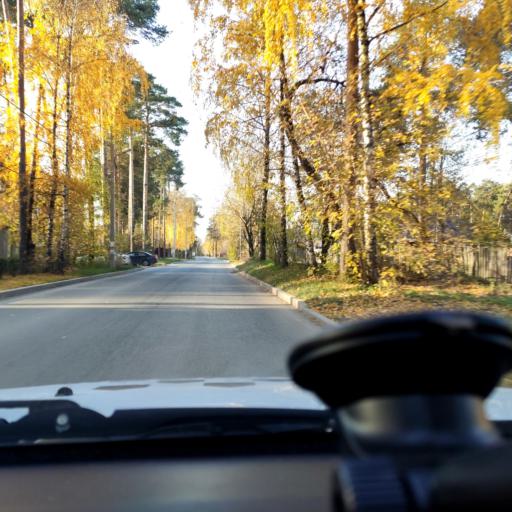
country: RU
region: Perm
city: Perm
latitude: 58.0508
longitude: 56.2907
